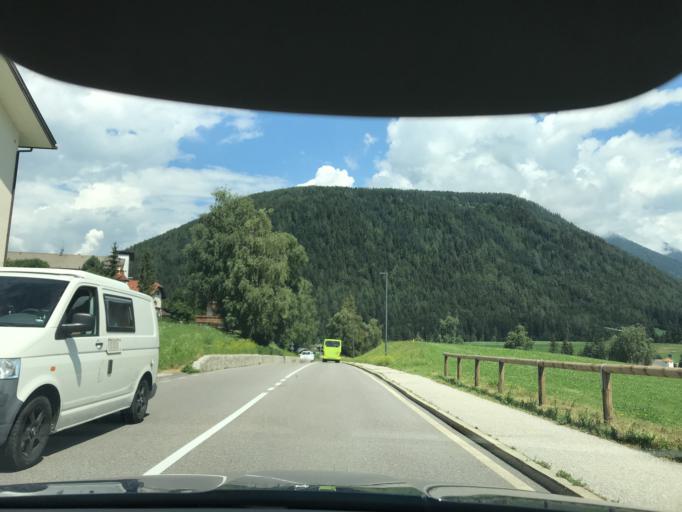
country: IT
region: Trentino-Alto Adige
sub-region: Bolzano
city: Valdaora di Mezzo
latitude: 46.7676
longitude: 12.0311
